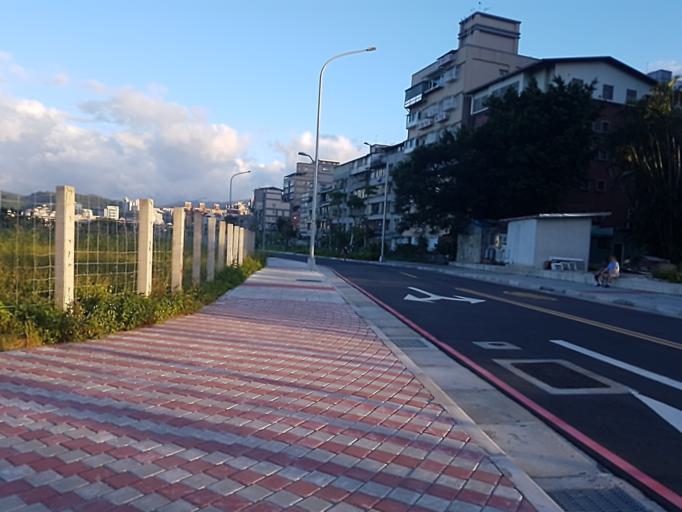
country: TW
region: Taipei
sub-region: Taipei
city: Banqiao
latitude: 24.9791
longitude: 121.5251
